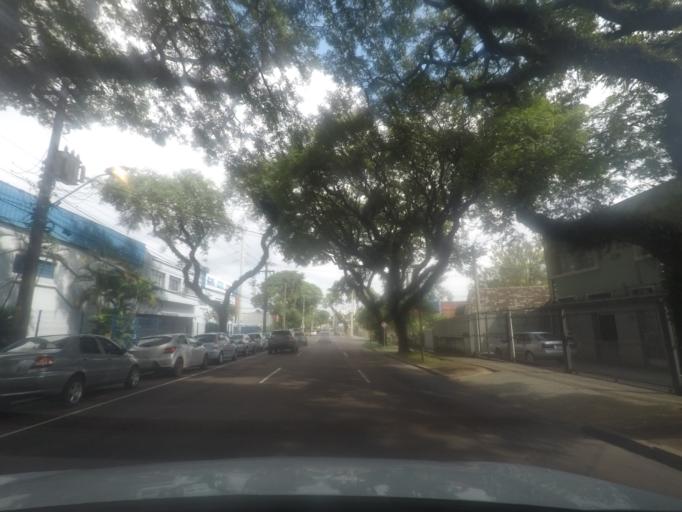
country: BR
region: Parana
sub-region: Curitiba
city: Curitiba
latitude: -25.4395
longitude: -49.2534
